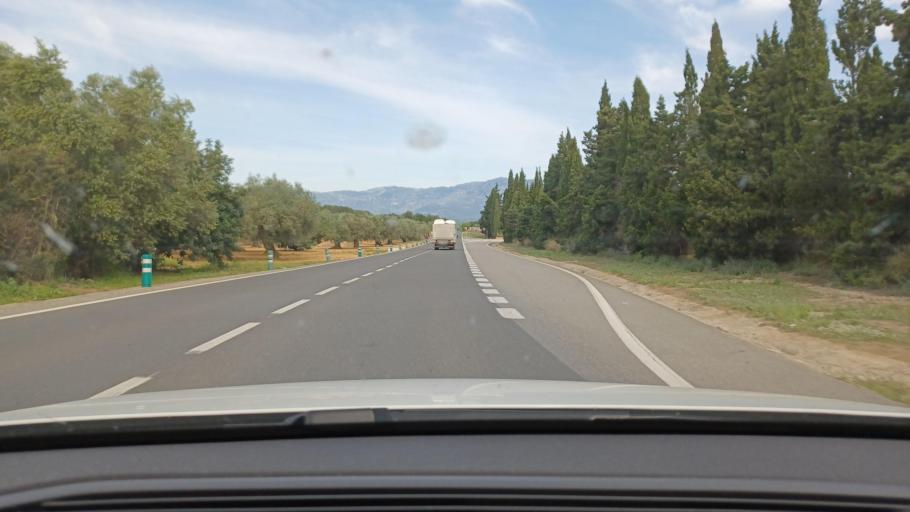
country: ES
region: Catalonia
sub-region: Provincia de Tarragona
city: Masdenverge
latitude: 40.7086
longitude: 0.5422
